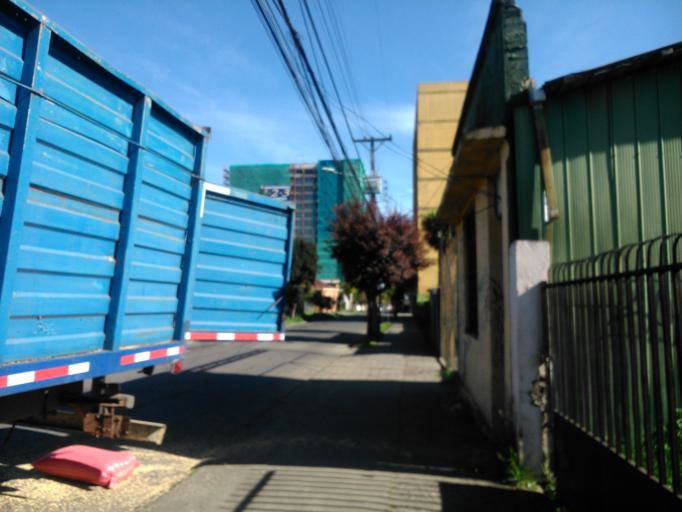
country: CL
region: Araucania
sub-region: Provincia de Cautin
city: Temuco
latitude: -38.7388
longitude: -72.5960
